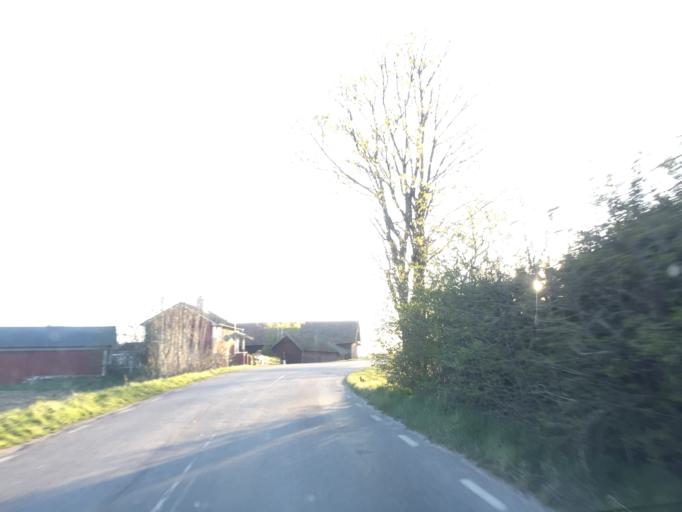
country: SE
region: OErebro
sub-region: Orebro Kommun
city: Odensbacken
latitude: 59.2049
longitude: 15.5220
